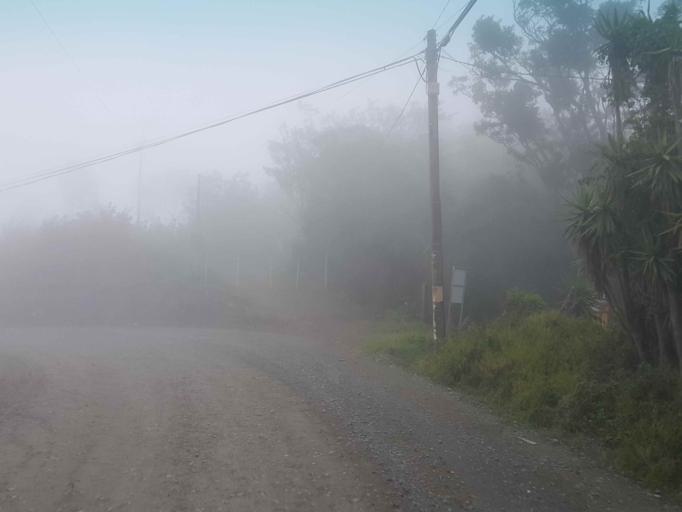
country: CR
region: Guanacaste
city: Juntas
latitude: 10.2948
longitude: -84.8332
